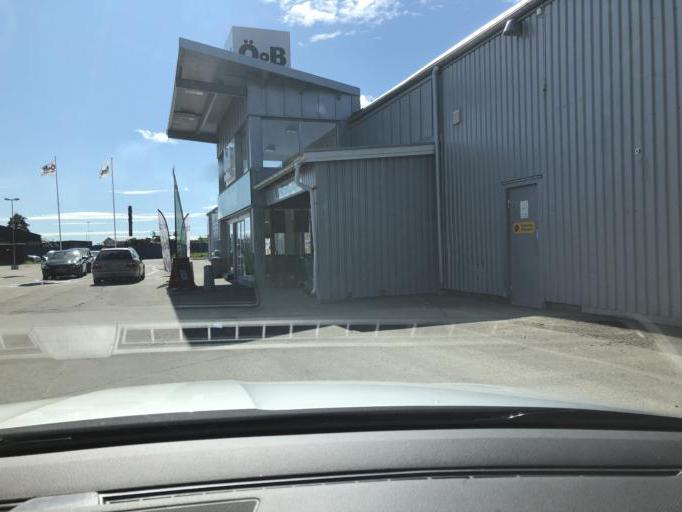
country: SE
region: Norrbotten
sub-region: Pitea Kommun
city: Pitea
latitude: 65.3232
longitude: 21.4355
